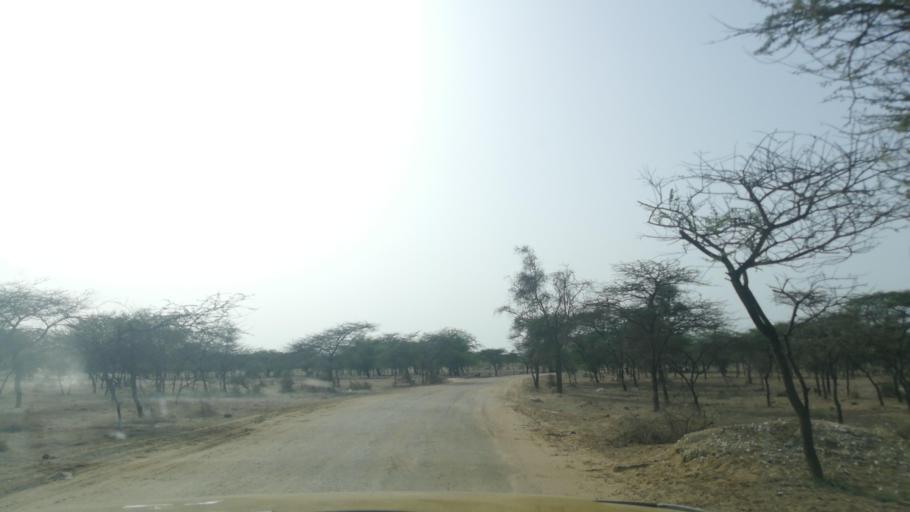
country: SN
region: Saint-Louis
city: Saint-Louis
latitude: 16.0610
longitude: -16.3337
